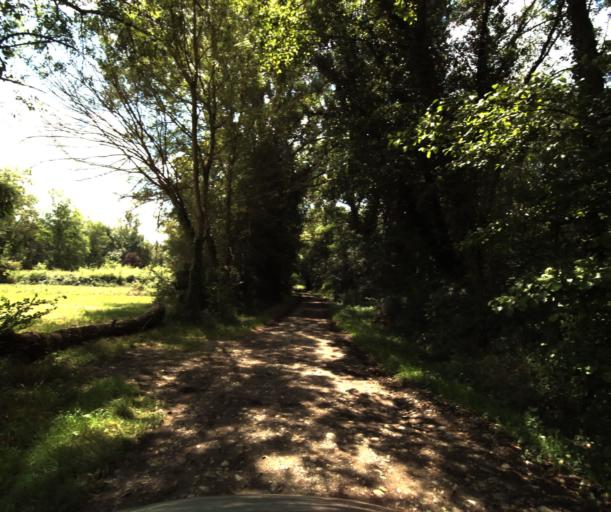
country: FR
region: Midi-Pyrenees
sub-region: Departement de la Haute-Garonne
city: Lacasse
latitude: 43.3954
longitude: 1.2729
